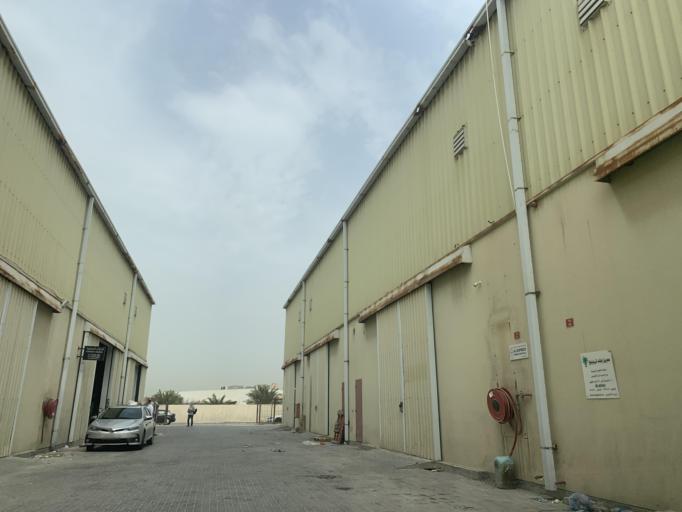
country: BH
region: Northern
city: Madinat `Isa
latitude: 26.1789
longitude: 50.5063
